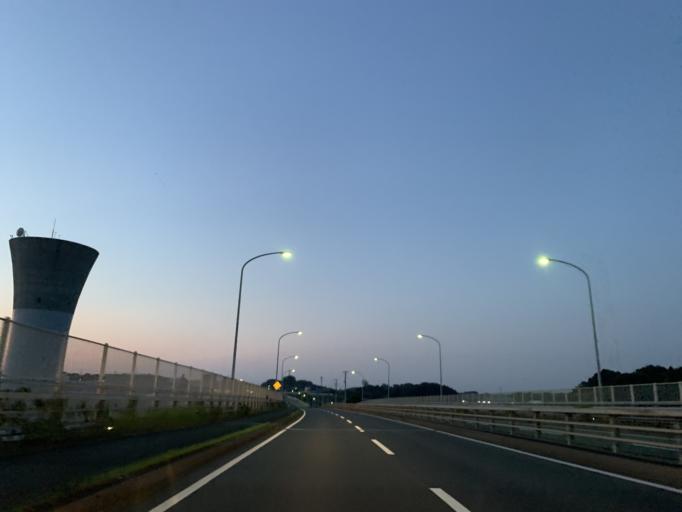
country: JP
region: Chiba
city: Nagareyama
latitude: 35.8713
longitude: 139.9080
